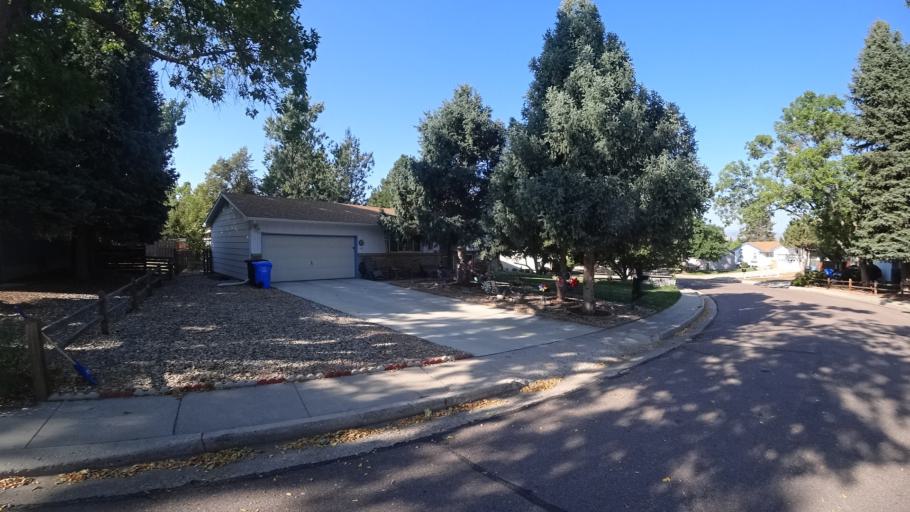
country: US
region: Colorado
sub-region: El Paso County
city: Cimarron Hills
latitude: 38.8781
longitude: -104.7434
